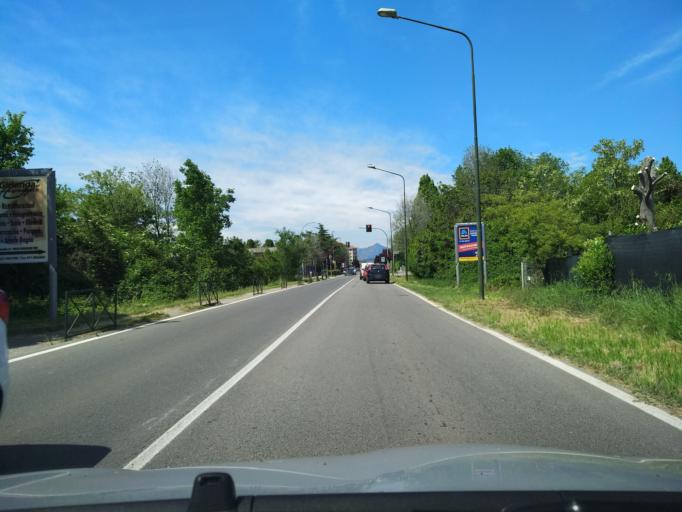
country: IT
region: Piedmont
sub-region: Provincia di Torino
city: Piossasco
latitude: 44.9860
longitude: 7.4687
